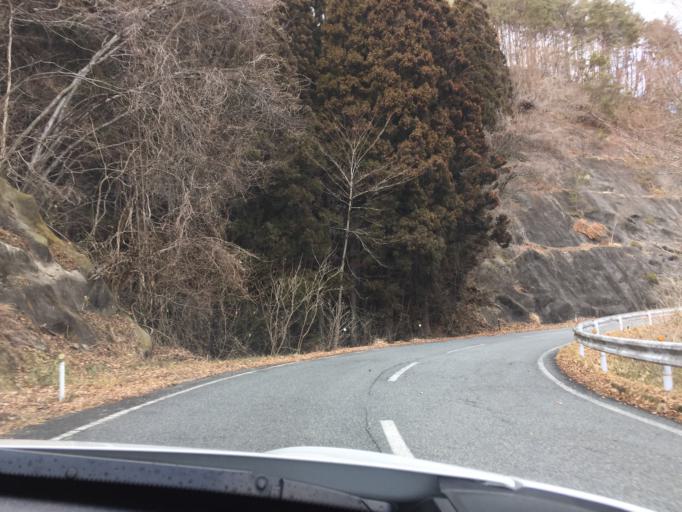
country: JP
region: Fukushima
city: Iwaki
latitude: 37.2112
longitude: 140.7454
